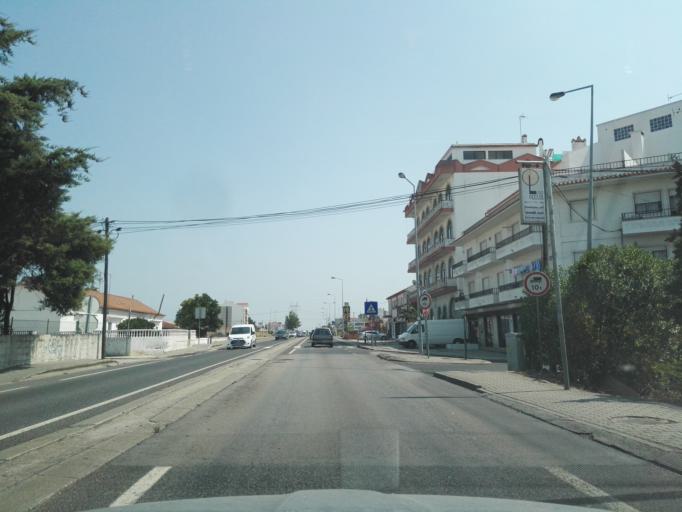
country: PT
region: Santarem
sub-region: Benavente
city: Samora Correia
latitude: 38.9230
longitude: -8.8862
